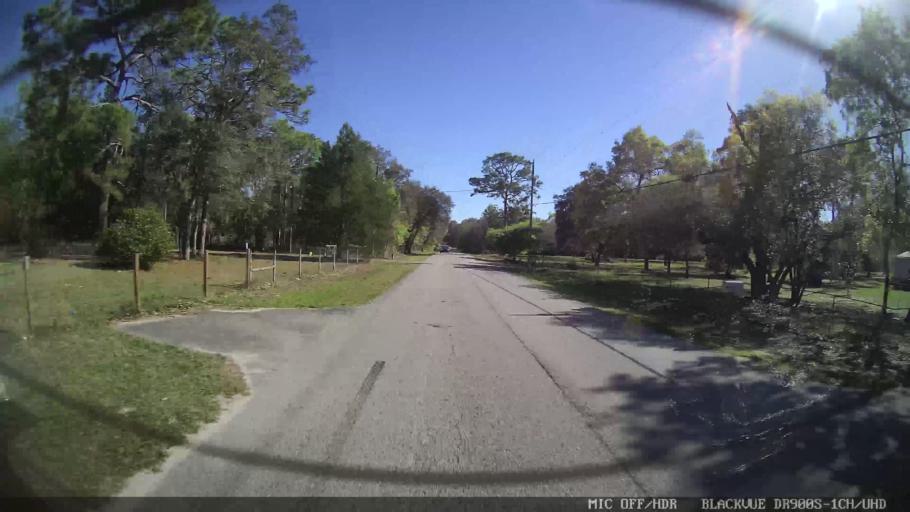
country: US
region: Florida
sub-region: Pasco County
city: Shady Hills
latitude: 28.4087
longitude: -82.5737
